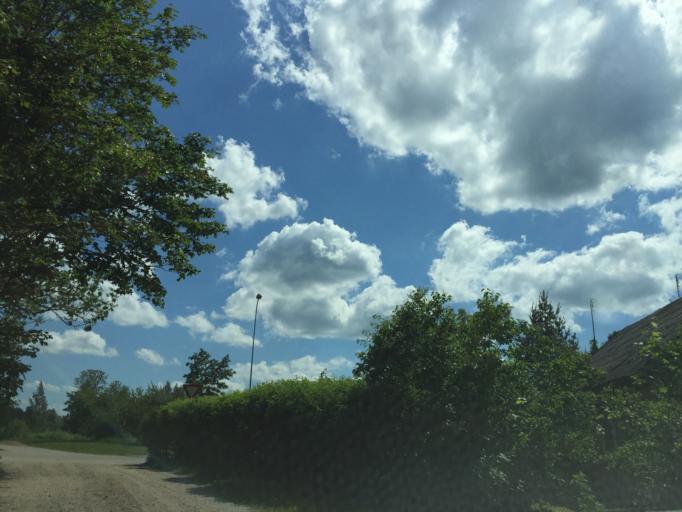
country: LV
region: Priekuli
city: Priekuli
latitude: 57.2625
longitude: 25.4293
